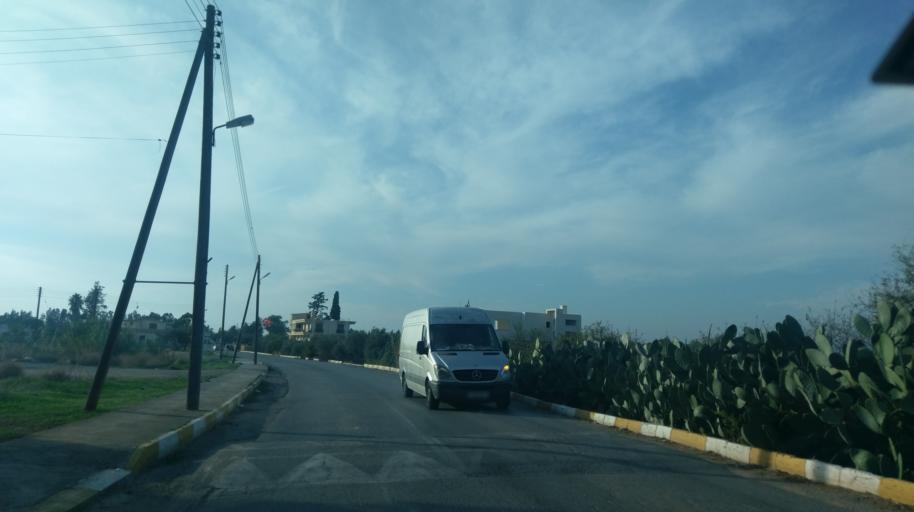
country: CY
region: Larnaka
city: Pergamos
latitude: 35.1058
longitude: 33.7146
